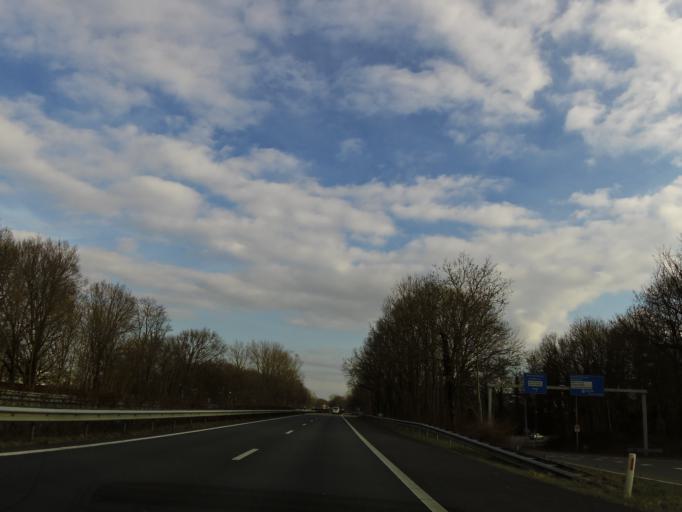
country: NL
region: Limburg
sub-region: Gemeente Heerlen
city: Nieuw-Lotbroek
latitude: 50.9020
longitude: 5.9337
